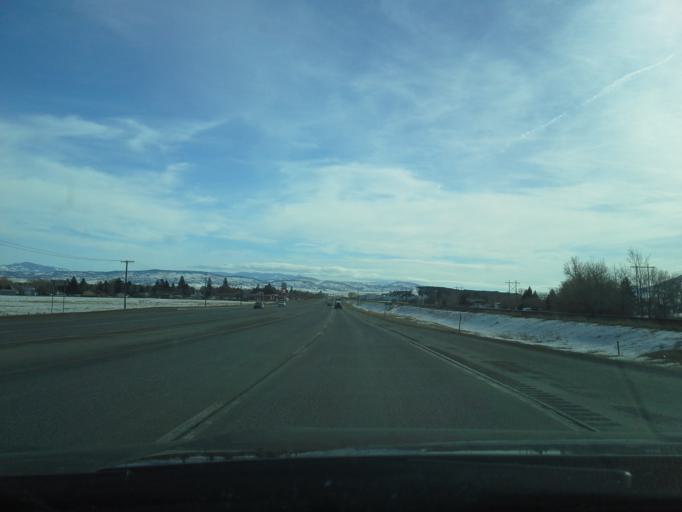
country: US
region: Montana
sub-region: Lewis and Clark County
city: East Helena
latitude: 46.5903
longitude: -111.9381
